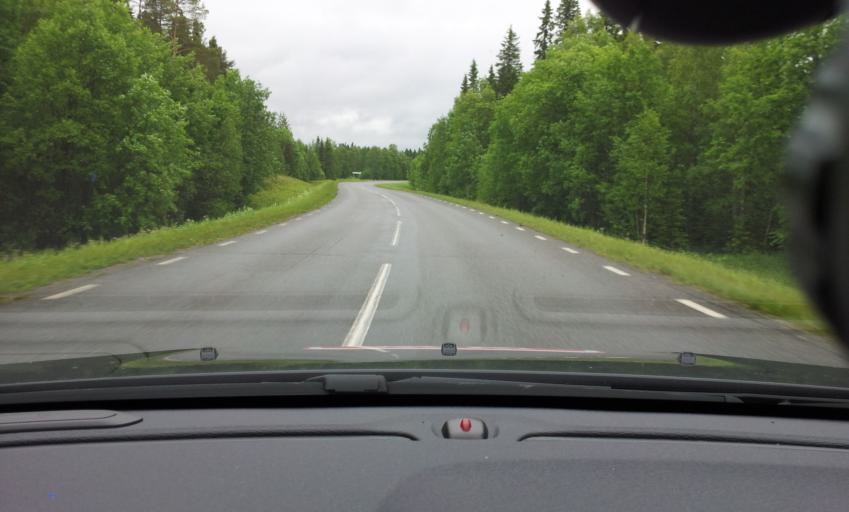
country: SE
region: Jaemtland
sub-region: Stroemsunds Kommun
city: Stroemsund
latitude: 63.5947
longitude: 15.3391
